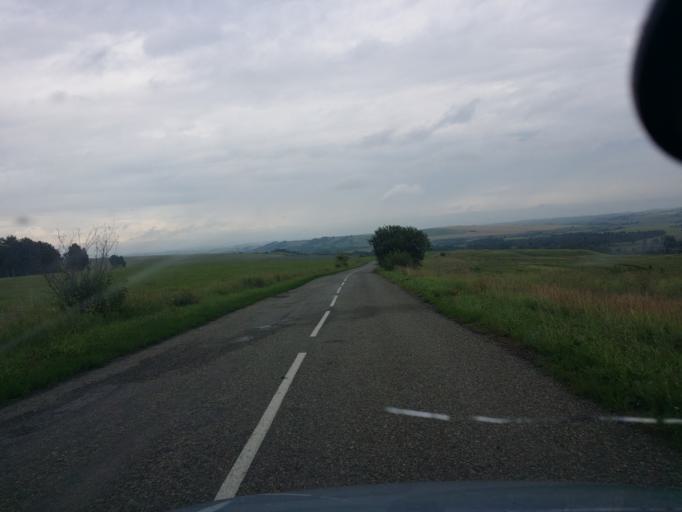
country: RU
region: Altai Krai
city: Verkh-Bekhtemir
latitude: 52.7478
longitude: 85.8418
